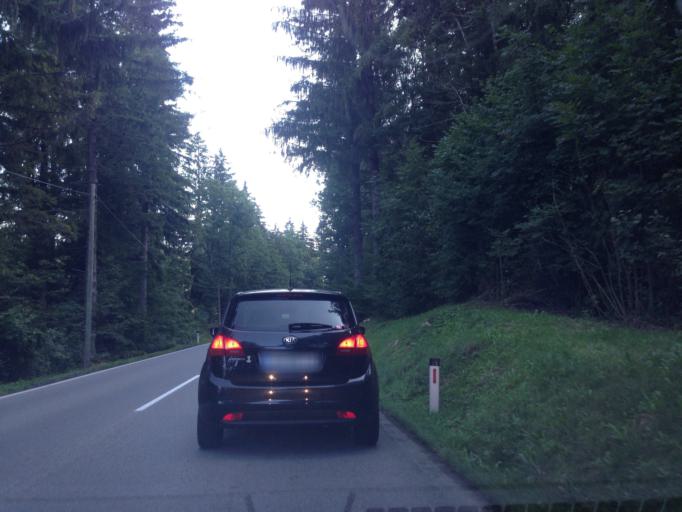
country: DE
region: Bavaria
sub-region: Swabia
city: Fuessen
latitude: 47.5545
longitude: 10.6825
